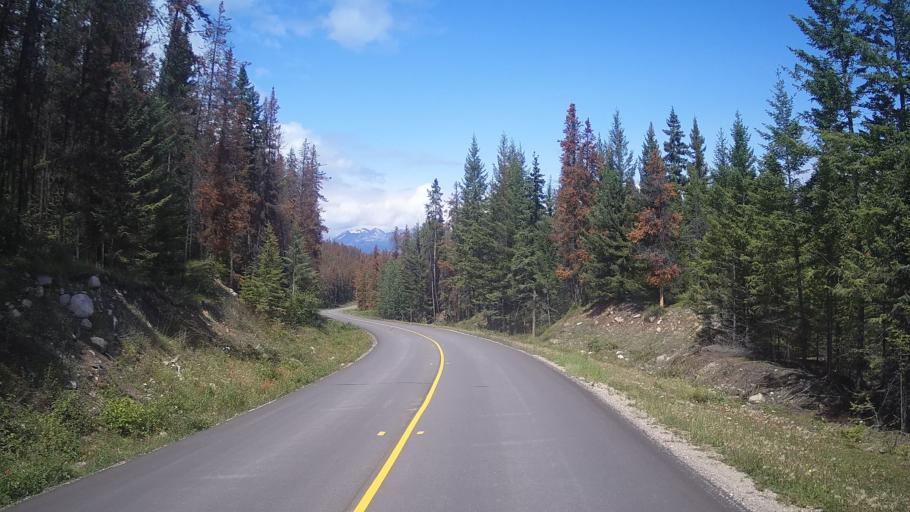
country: CA
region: Alberta
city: Jasper Park Lodge
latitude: 52.7875
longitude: -118.0336
